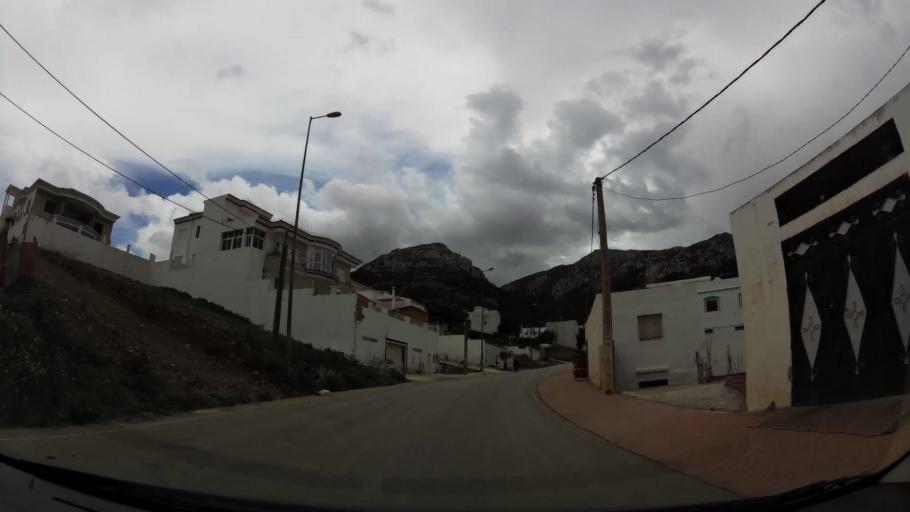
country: MA
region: Tanger-Tetouan
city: Tetouan
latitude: 35.5515
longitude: -5.3682
